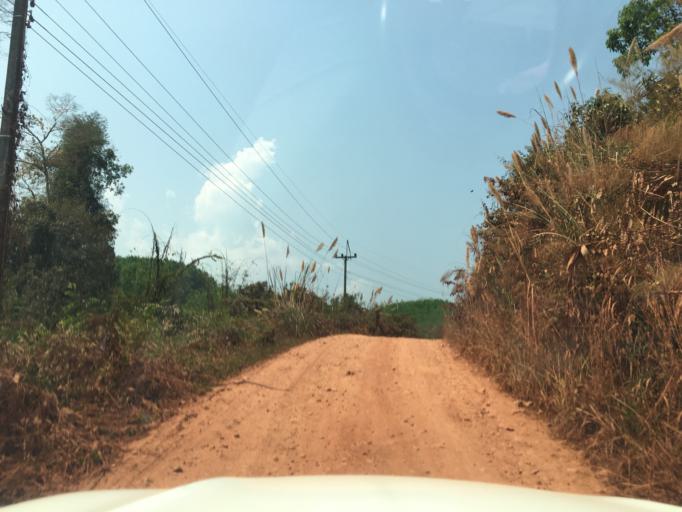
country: LA
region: Bolikhamxai
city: Bolikhan
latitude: 18.7300
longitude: 103.6332
